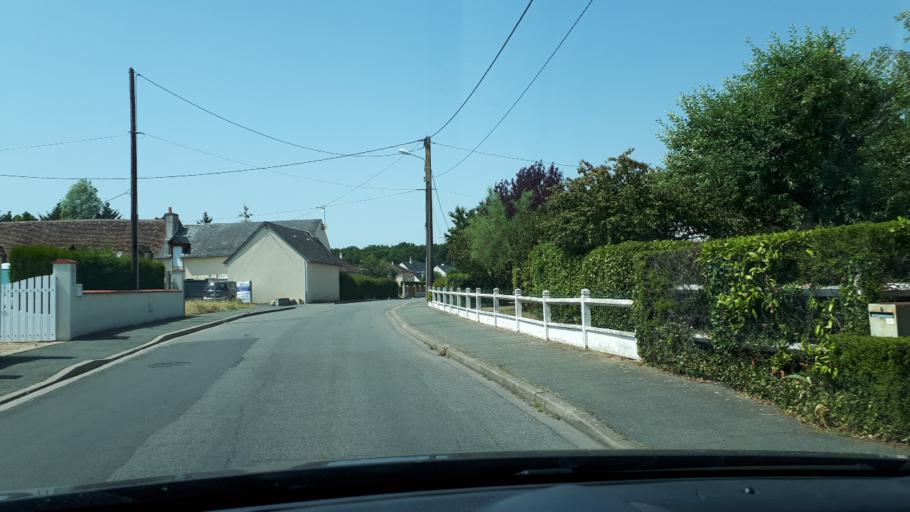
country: FR
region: Centre
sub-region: Departement du Loir-et-Cher
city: Vendome
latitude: 47.8126
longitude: 1.0488
